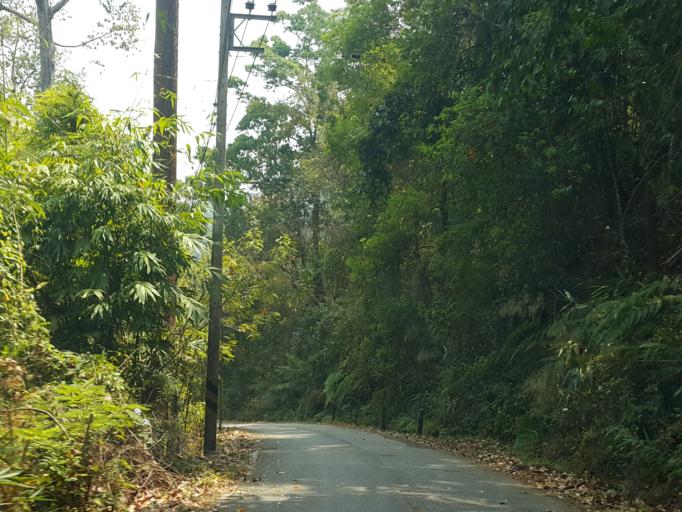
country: TH
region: Lampang
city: Mueang Pan
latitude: 18.8192
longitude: 99.4338
